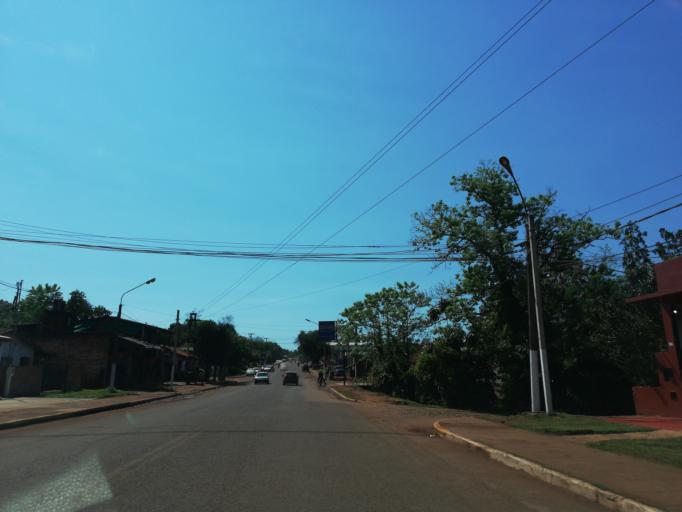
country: AR
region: Misiones
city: Puerto Eldorado
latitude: -26.4071
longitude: -54.6616
